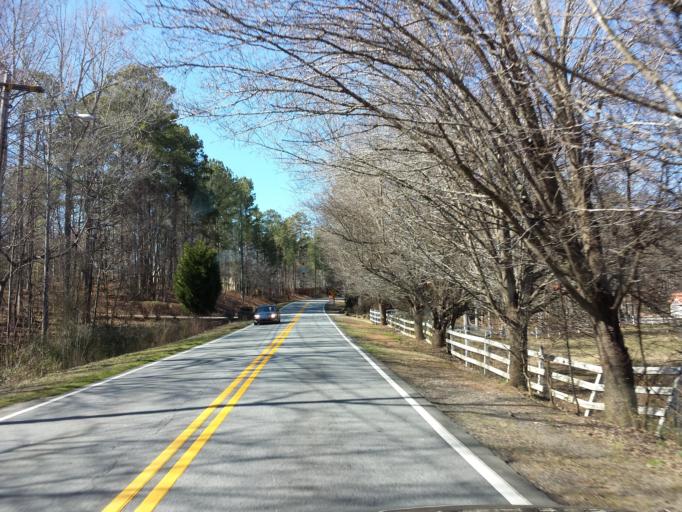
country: US
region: Georgia
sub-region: Cobb County
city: Fair Oaks
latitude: 33.9176
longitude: -84.6187
